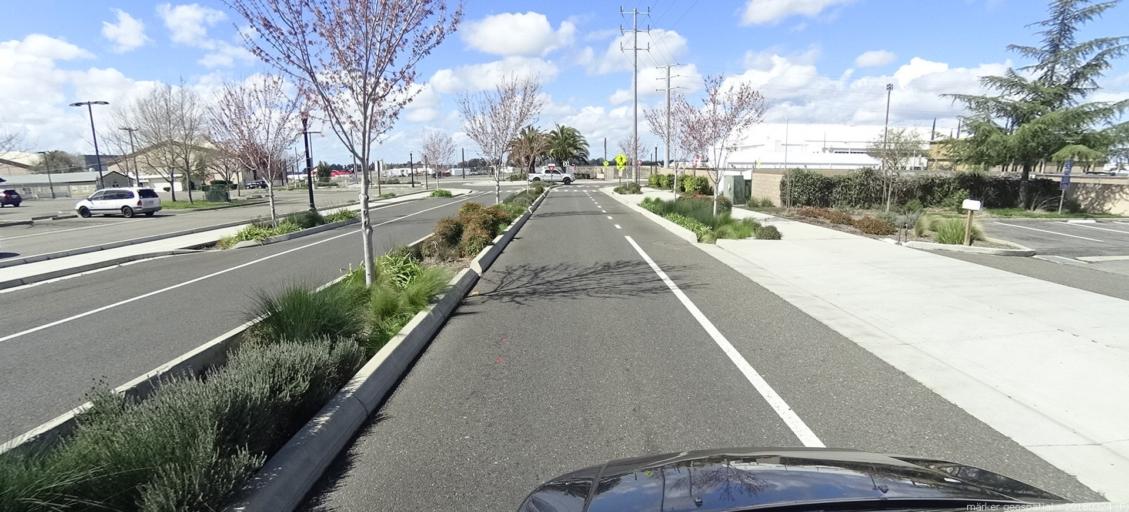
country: US
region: California
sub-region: Sacramento County
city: North Highlands
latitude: 38.6758
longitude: -121.3912
